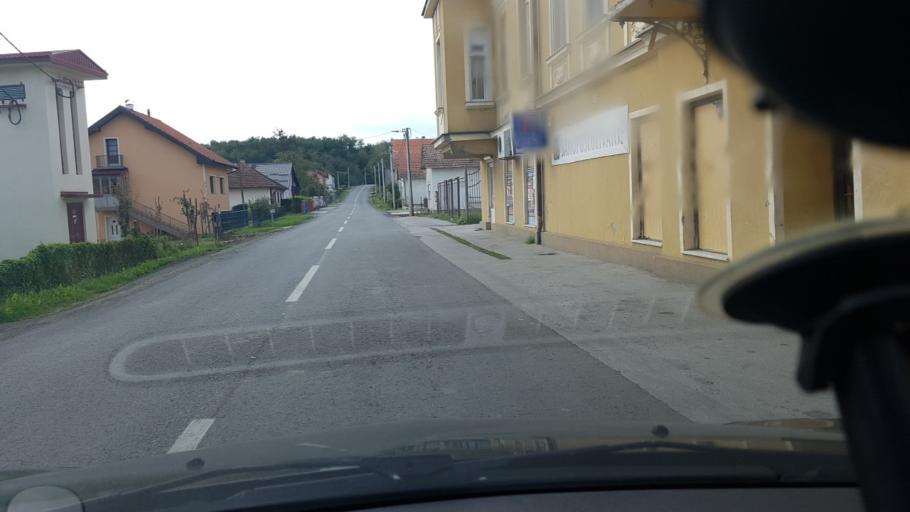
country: HR
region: Varazdinska
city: Ljubescica
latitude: 46.1098
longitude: 16.3905
